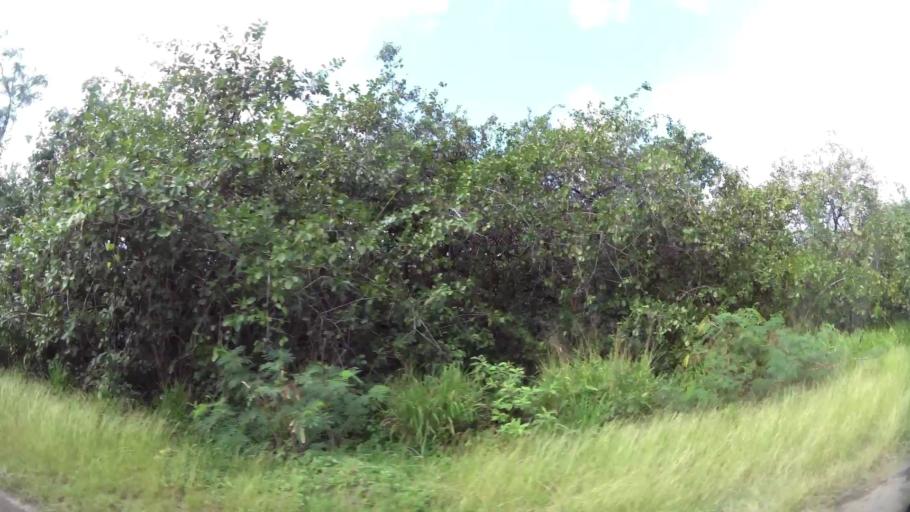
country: KN
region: Saint Thomas Lowland
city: Cotton Ground
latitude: 17.1779
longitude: -62.6229
